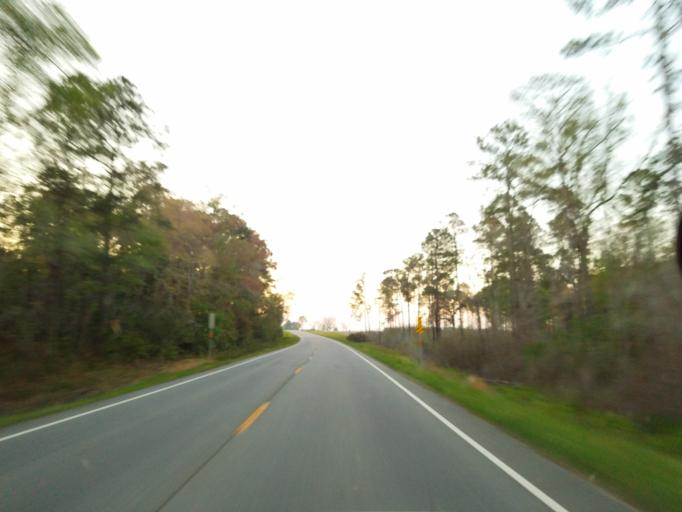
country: US
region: Georgia
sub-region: Berrien County
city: Nashville
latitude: 31.2760
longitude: -83.3274
